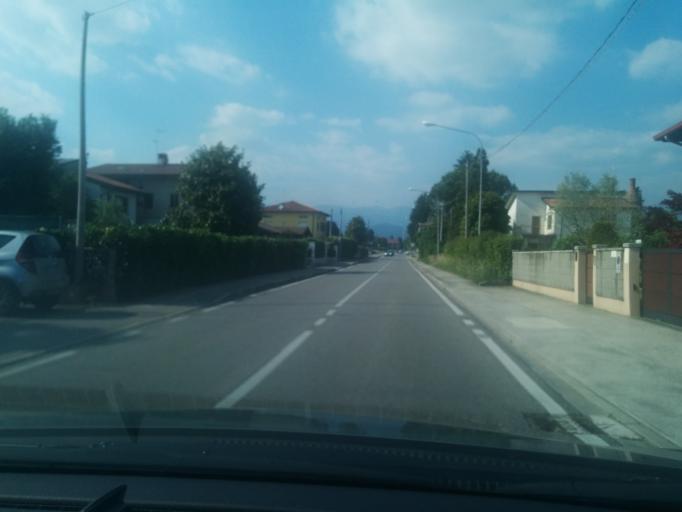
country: IT
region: Friuli Venezia Giulia
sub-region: Provincia di Udine
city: Reana del Rojale
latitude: 46.1426
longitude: 13.2439
